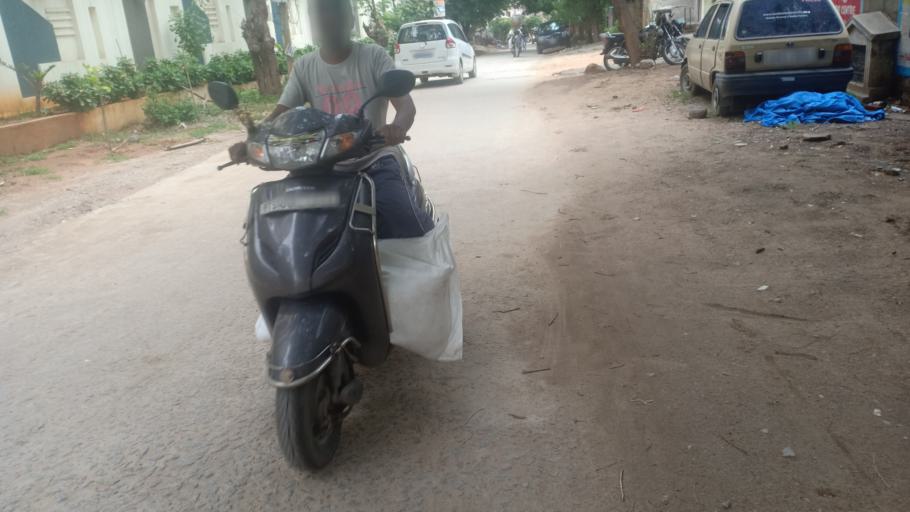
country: IN
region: Telangana
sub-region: Rangareddi
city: Uppal Kalan
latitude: 17.4115
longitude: 78.5705
